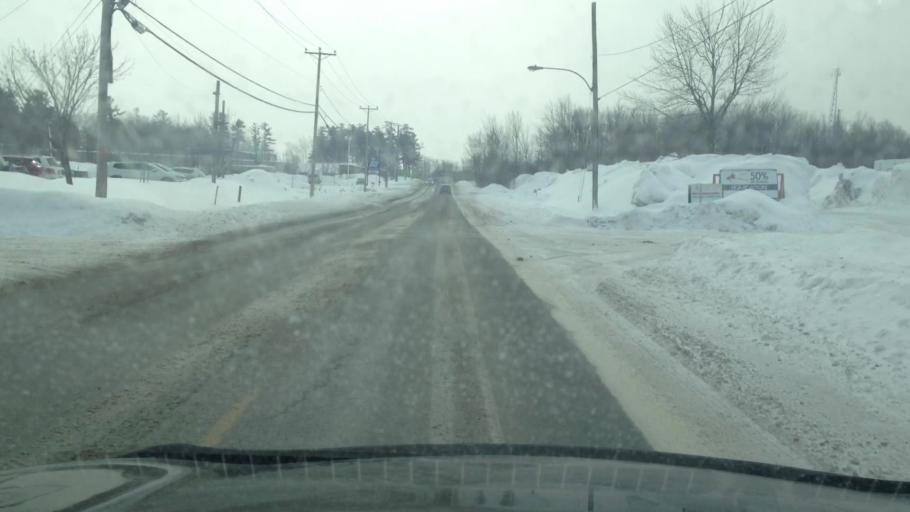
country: CA
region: Quebec
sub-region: Laurentides
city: Saint-Jerome
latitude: 45.7834
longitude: -74.0293
